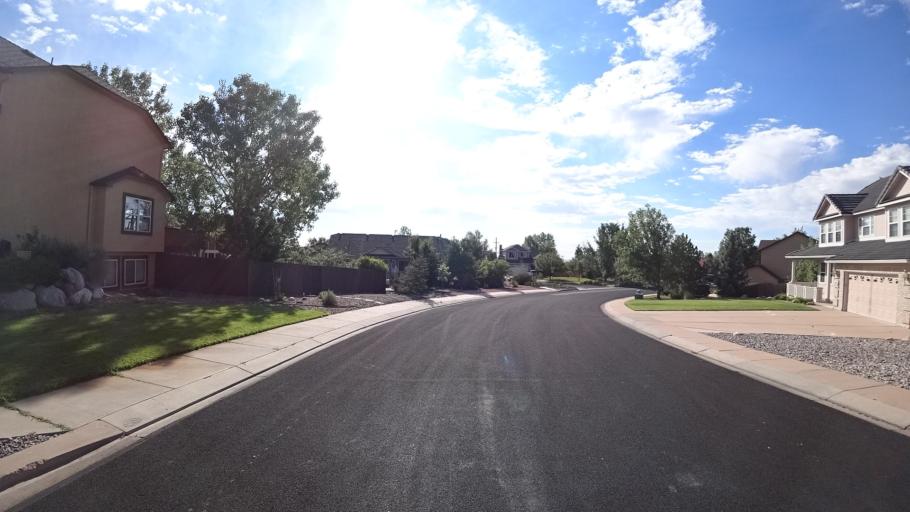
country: US
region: Colorado
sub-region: El Paso County
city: Fort Carson
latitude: 38.7536
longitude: -104.8132
